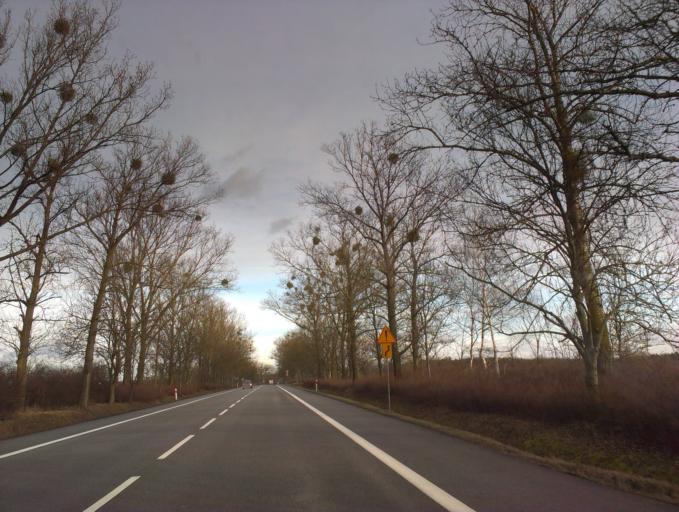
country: PL
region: Kujawsko-Pomorskie
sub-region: Powiat lipnowski
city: Lipno
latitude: 52.8575
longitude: 19.2409
